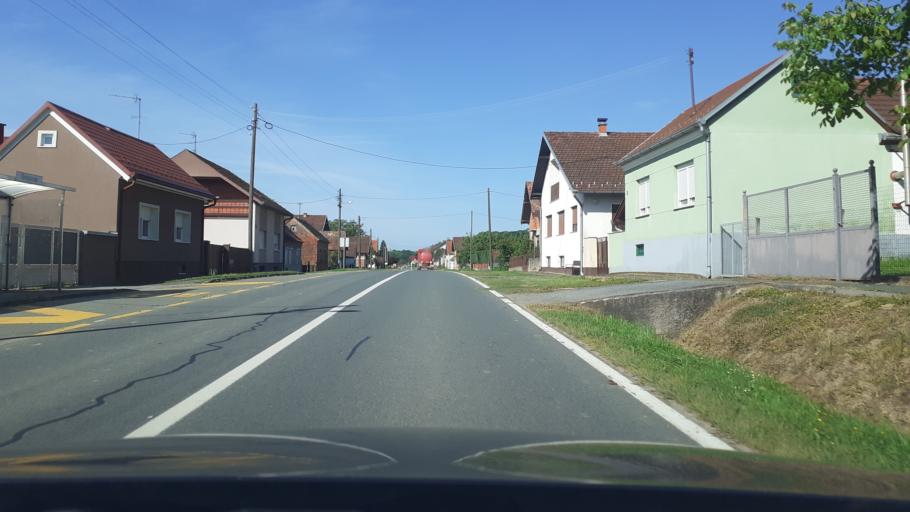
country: HR
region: Brodsko-Posavska
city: Batrina
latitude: 45.2149
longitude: 17.6969
